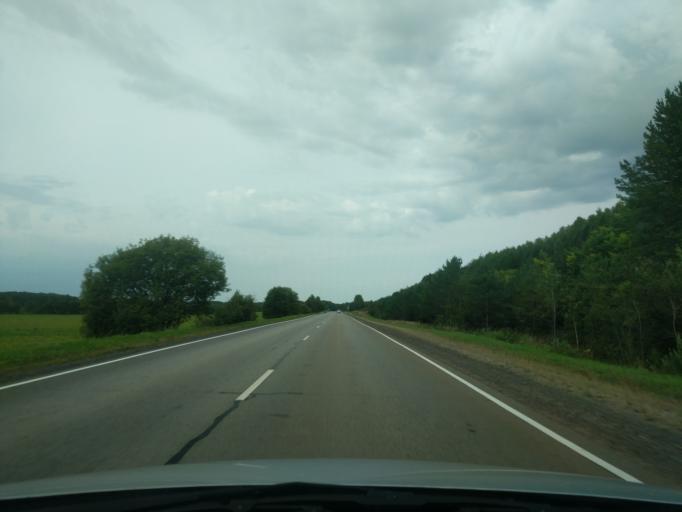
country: RU
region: Kirov
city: Svecha
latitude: 58.2734
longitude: 47.7470
